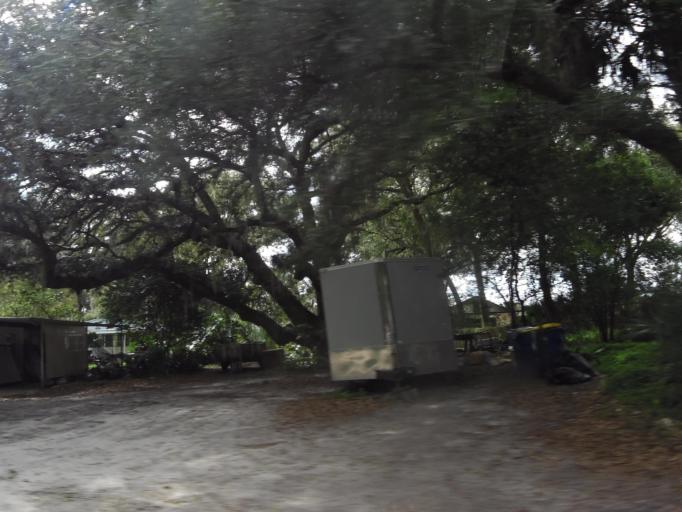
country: US
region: Florida
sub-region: Duval County
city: Jacksonville
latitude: 30.3261
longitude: -81.6030
